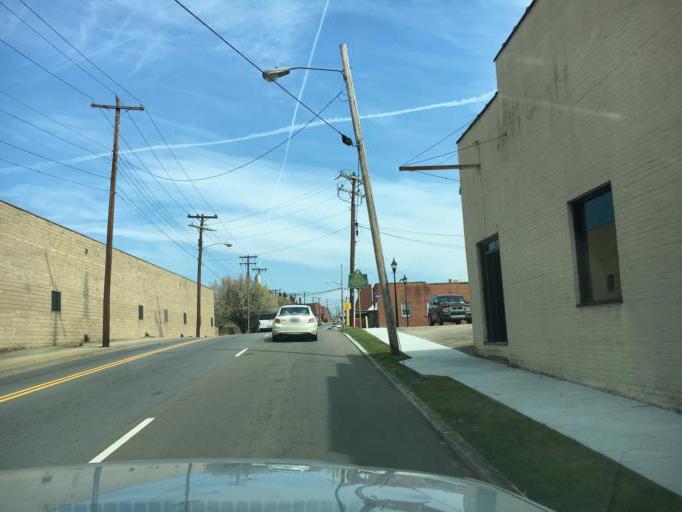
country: US
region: North Carolina
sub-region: McDowell County
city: Marion
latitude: 35.6817
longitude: -82.0114
